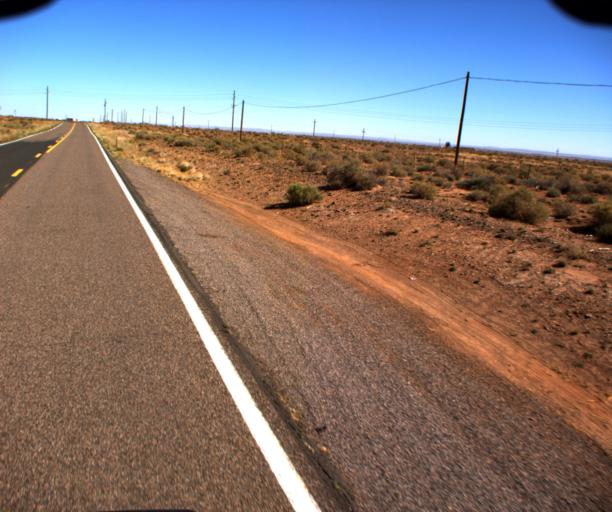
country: US
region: Arizona
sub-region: Coconino County
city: LeChee
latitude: 35.0799
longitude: -110.8606
